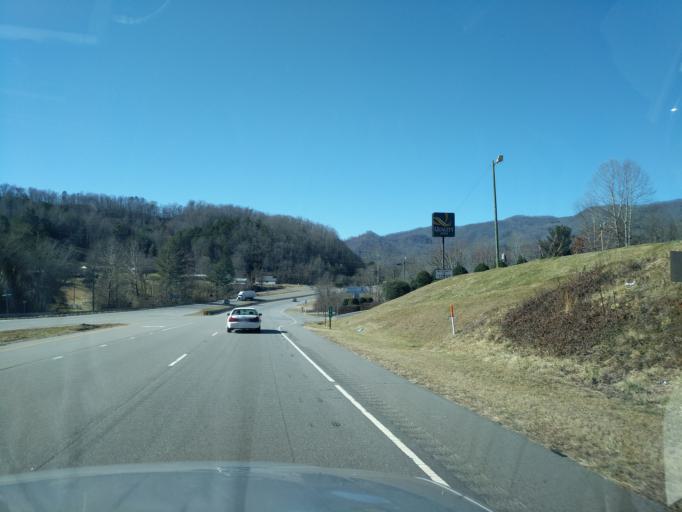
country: US
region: North Carolina
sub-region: Jackson County
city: Sylva
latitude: 35.3917
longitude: -83.1829
